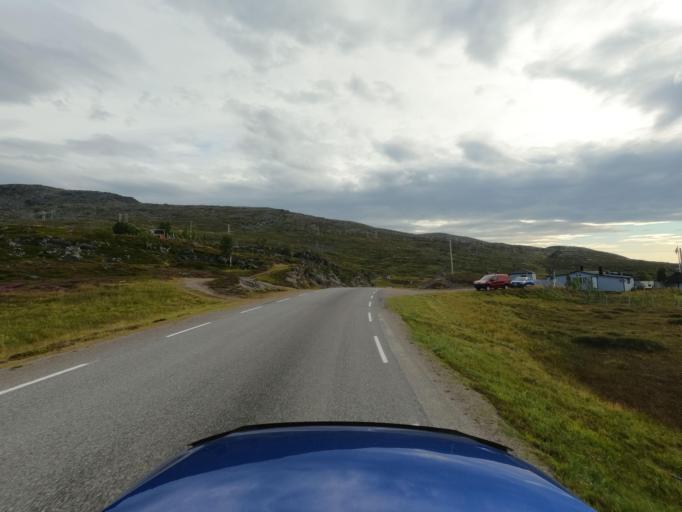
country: NO
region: Finnmark Fylke
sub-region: Hammerfest
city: Rypefjord
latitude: 70.6023
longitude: 23.6862
